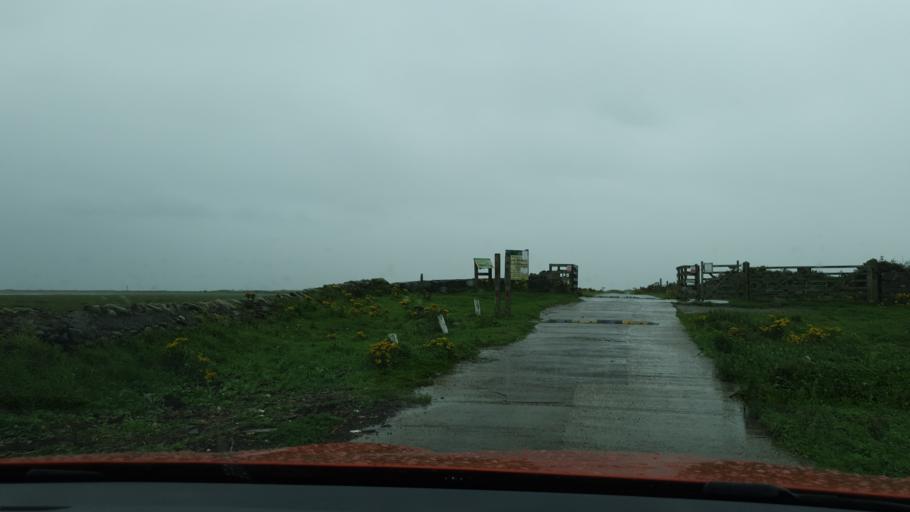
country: GB
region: England
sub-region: Cumbria
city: Barrow in Furness
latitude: 54.0512
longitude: -3.2041
